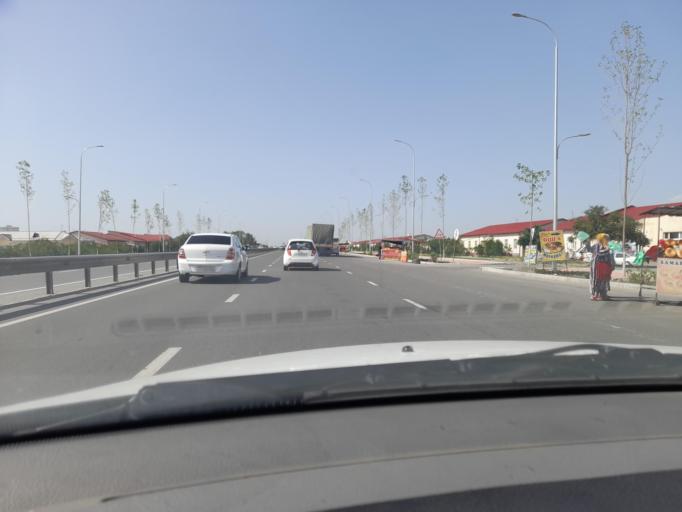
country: UZ
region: Samarqand
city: Samarqand
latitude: 39.7094
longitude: 66.9500
